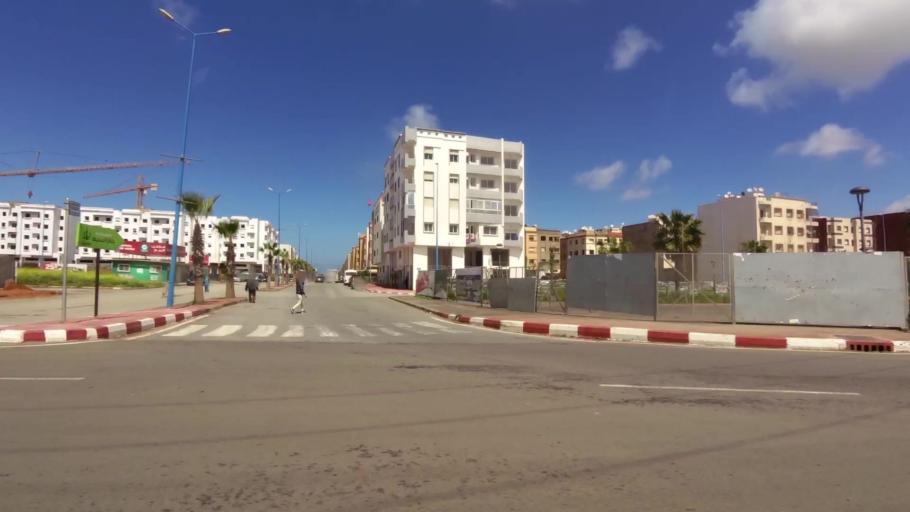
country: MA
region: Grand Casablanca
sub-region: Nouaceur
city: Dar Bouazza
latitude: 33.5313
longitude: -7.7293
